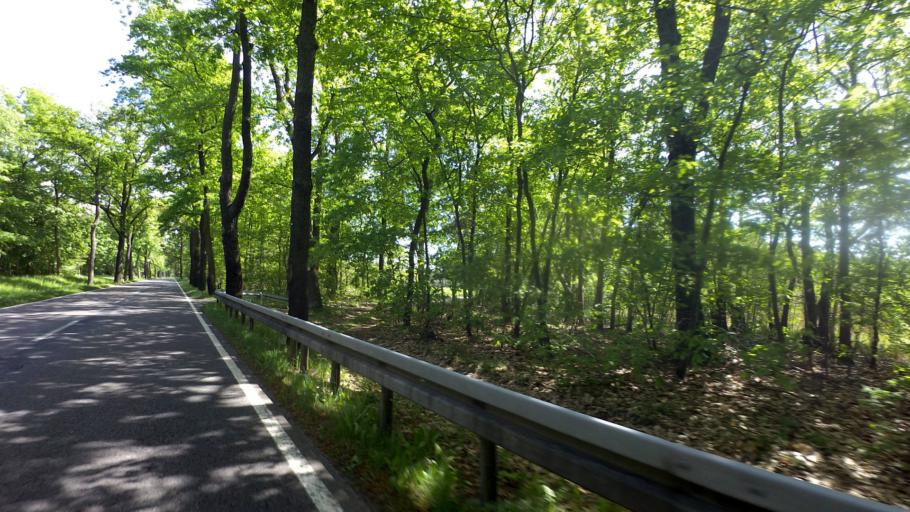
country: DE
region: Brandenburg
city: Sperenberg
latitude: 52.0481
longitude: 13.2899
